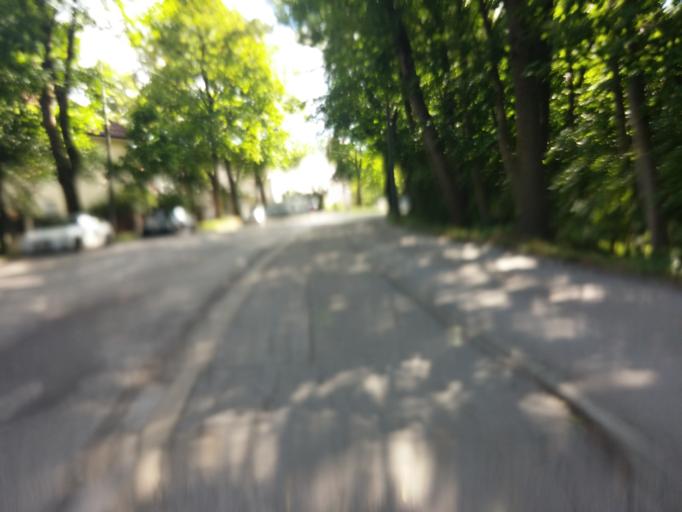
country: DE
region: Bavaria
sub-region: Upper Bavaria
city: Bogenhausen
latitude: 48.1535
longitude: 11.6112
